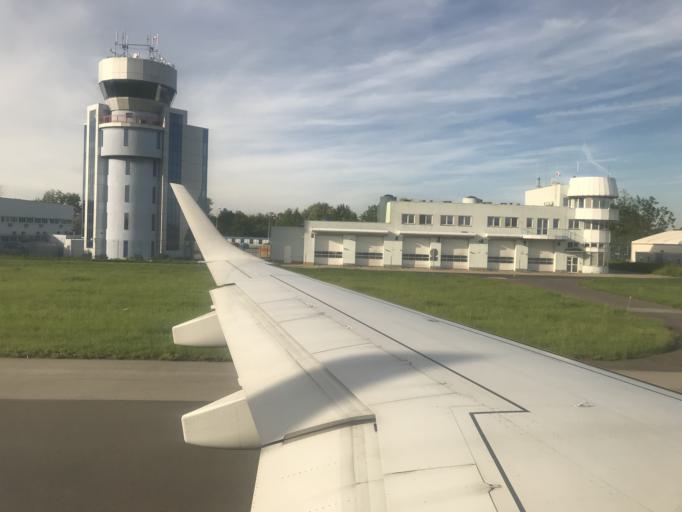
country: PL
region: Lower Silesian Voivodeship
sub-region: Powiat wroclawski
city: Smolec
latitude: 51.1062
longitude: 16.8862
